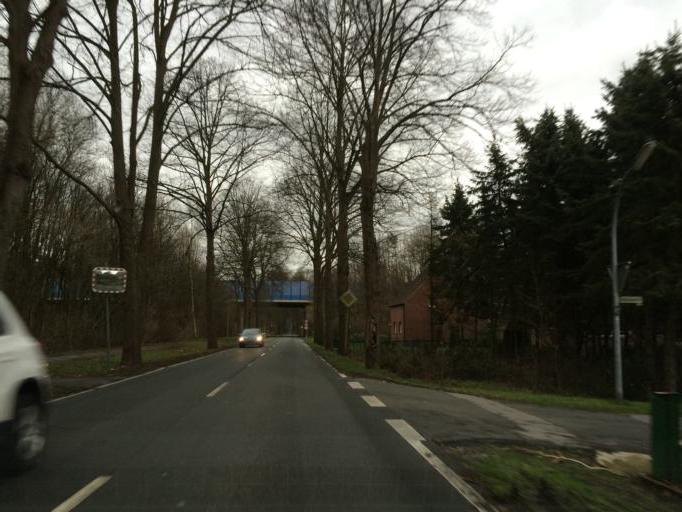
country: DE
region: North Rhine-Westphalia
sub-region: Regierungsbezirk Munster
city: Haltern
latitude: 51.7228
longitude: 7.1481
